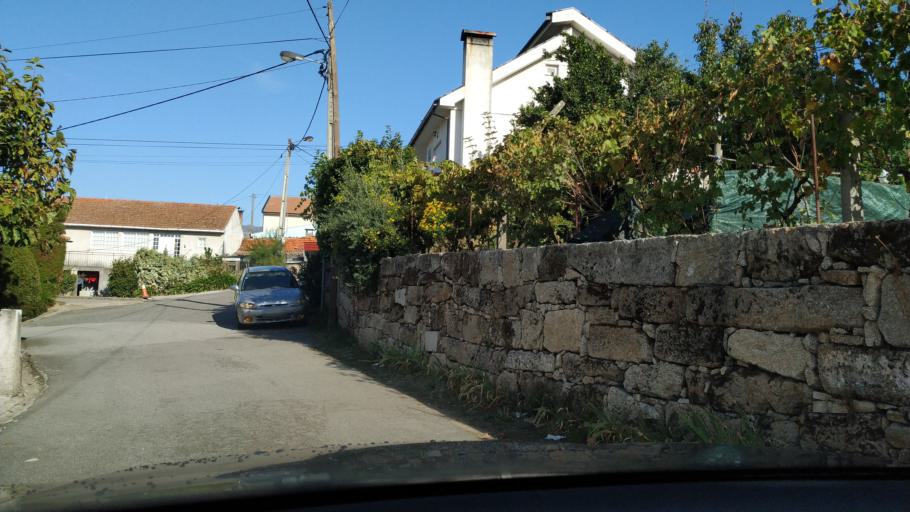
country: PT
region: Vila Real
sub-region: Vila Real
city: Vila Real
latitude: 41.3191
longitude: -7.7098
